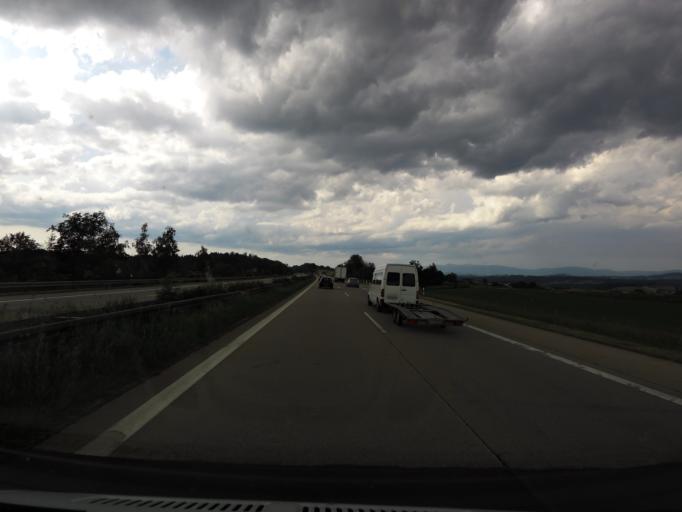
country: DE
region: Bavaria
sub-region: Lower Bavaria
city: Iggensbach
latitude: 48.7322
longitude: 13.1309
